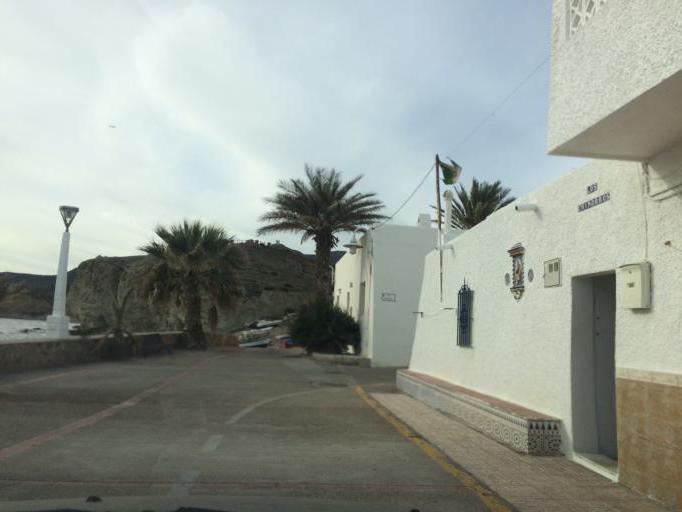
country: ES
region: Andalusia
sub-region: Provincia de Almeria
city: San Jose
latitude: 36.8136
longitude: -2.0520
